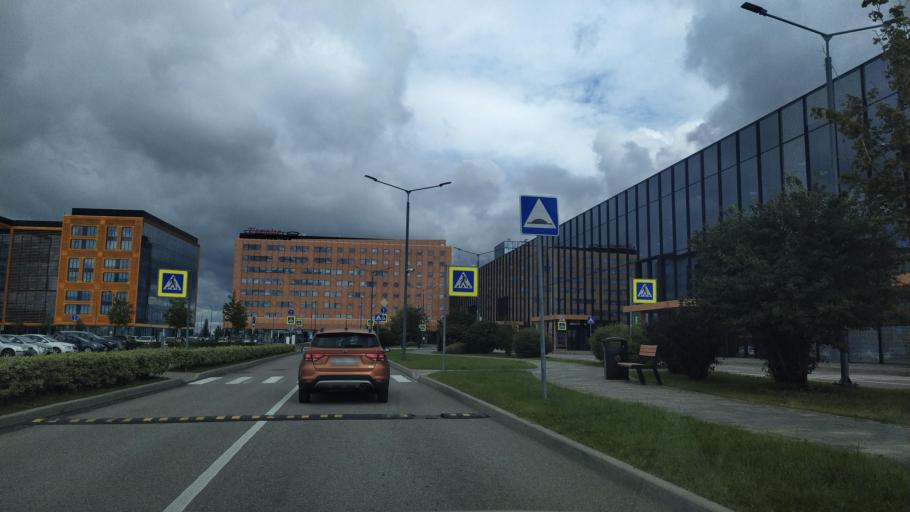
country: RU
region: St.-Petersburg
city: Aleksandrovskaya
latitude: 59.7620
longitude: 30.3540
